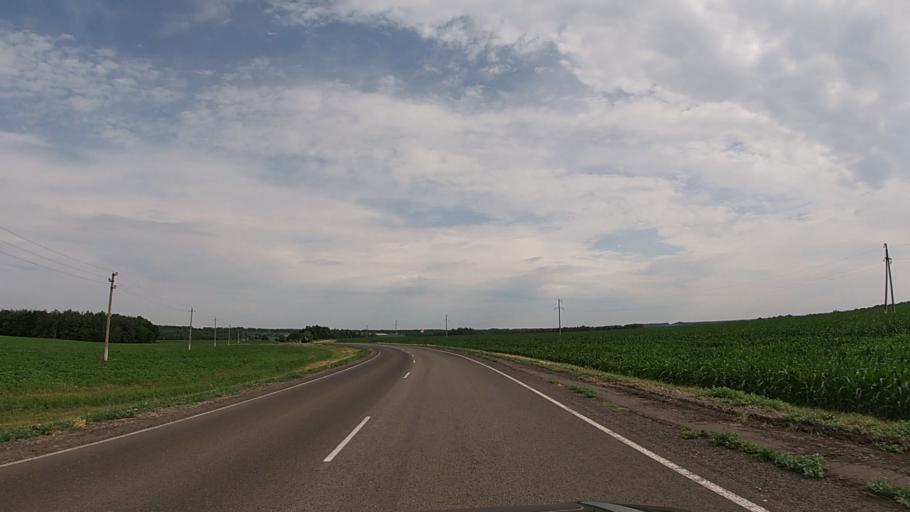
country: RU
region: Belgorod
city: Krasnaya Yaruga
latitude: 50.8199
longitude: 35.5017
